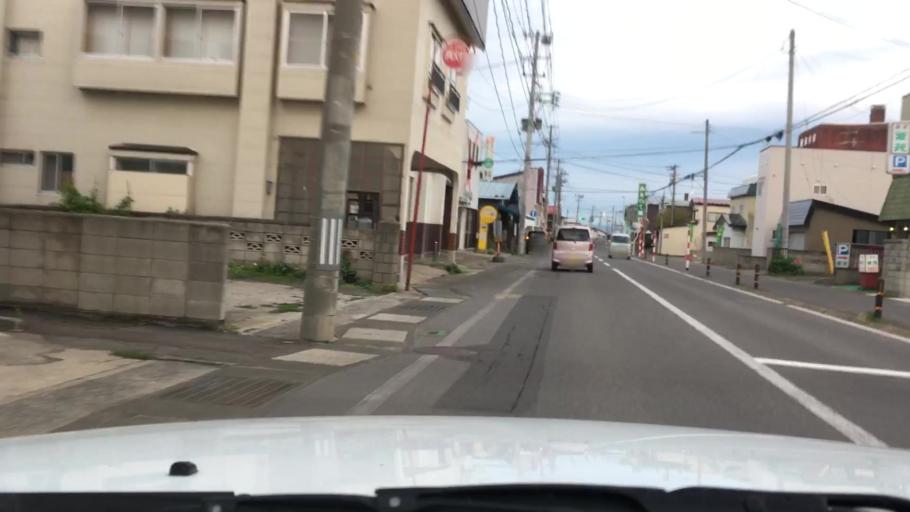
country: JP
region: Aomori
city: Hirosaki
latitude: 40.5890
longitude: 140.4816
